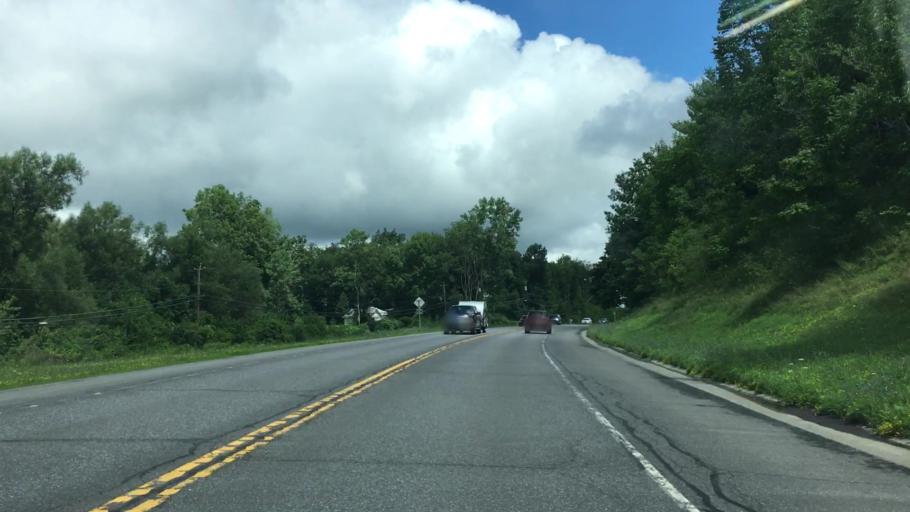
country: US
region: New York
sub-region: Rensselaer County
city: Poestenkill
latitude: 42.7750
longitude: -73.5881
